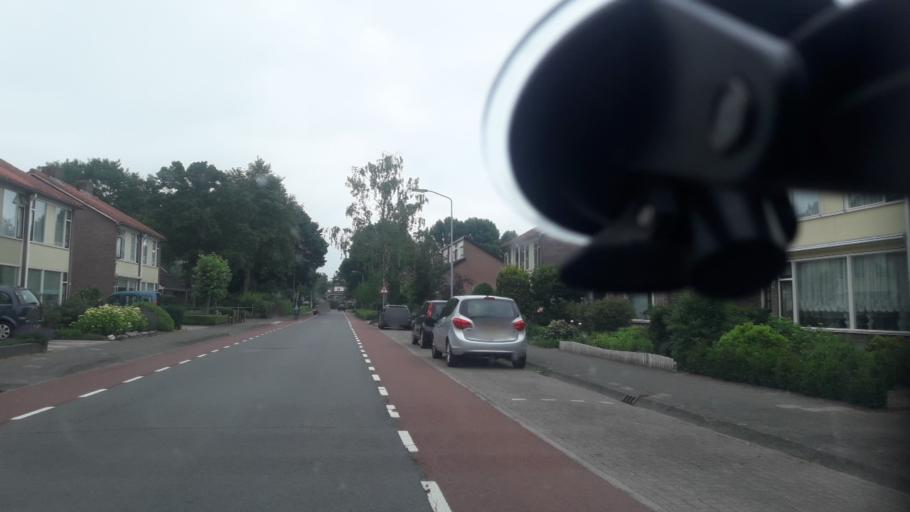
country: NL
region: Gelderland
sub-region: Gemeente Elburg
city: Elburg
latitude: 52.4443
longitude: 5.8513
